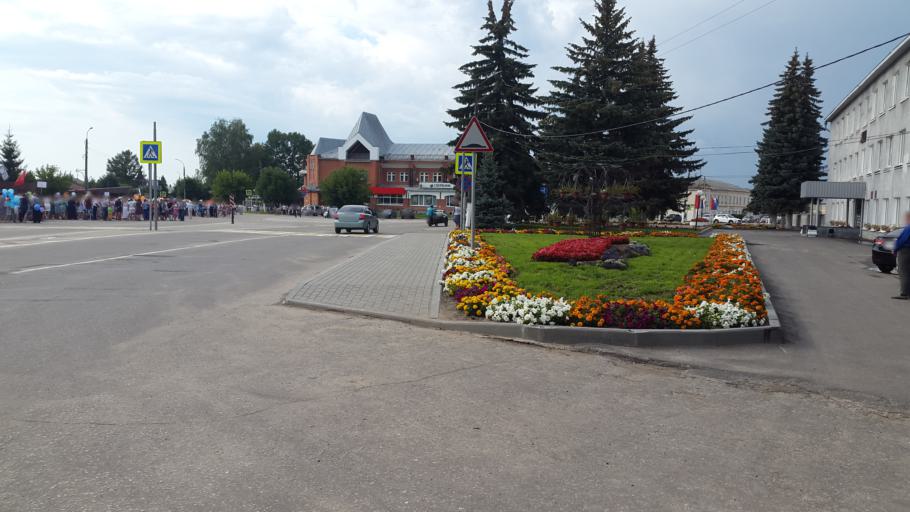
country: RU
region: Vladimir
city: Gorokhovets
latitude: 56.2010
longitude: 42.6921
